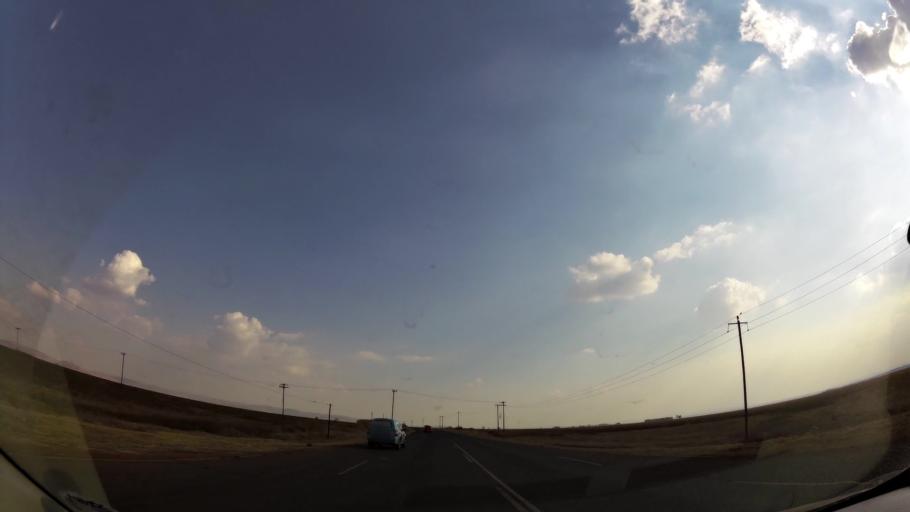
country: ZA
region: Gauteng
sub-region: Sedibeng District Municipality
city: Heidelberg
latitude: -26.3893
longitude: 28.2963
